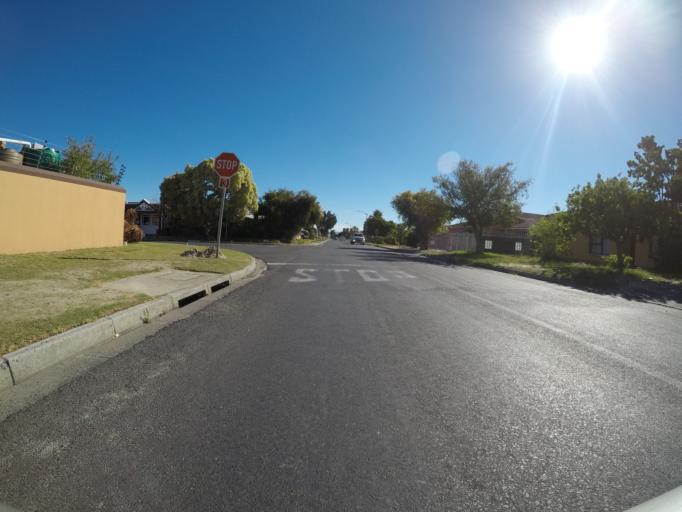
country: ZA
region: Western Cape
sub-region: City of Cape Town
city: Kraaifontein
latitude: -33.9446
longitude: 18.6827
